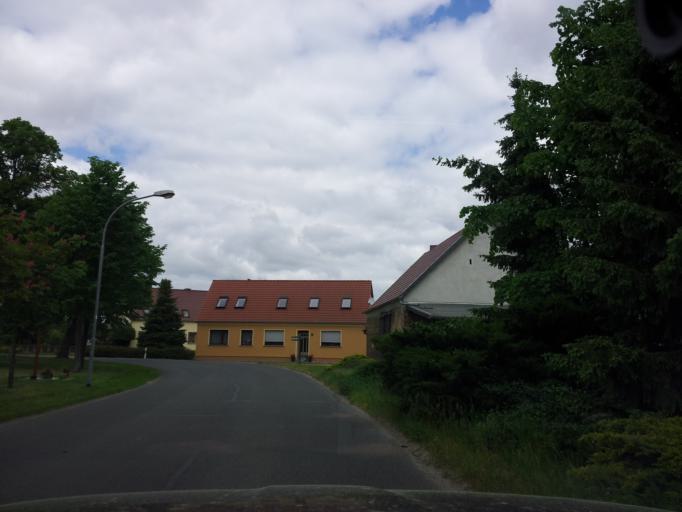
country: DE
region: Brandenburg
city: Treuenbrietzen
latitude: 52.0754
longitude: 12.8100
